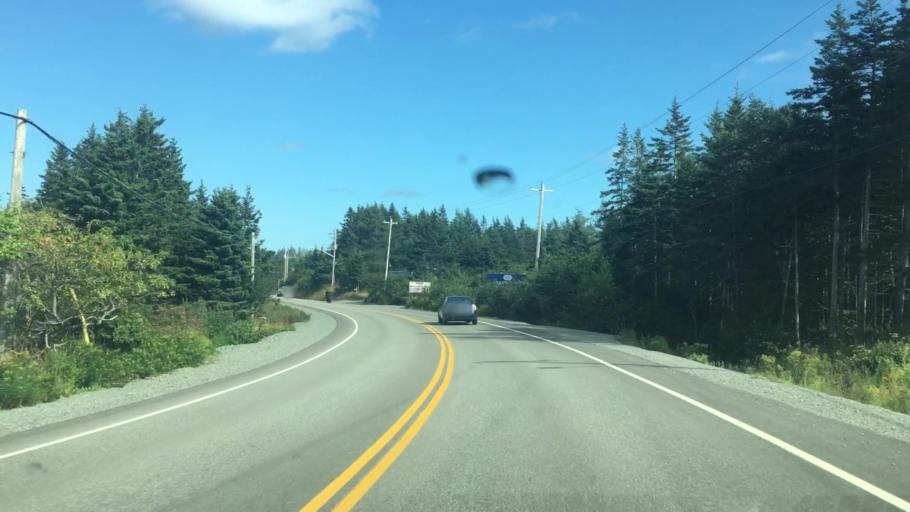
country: CA
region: Nova Scotia
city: Princeville
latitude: 45.6506
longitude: -60.8522
